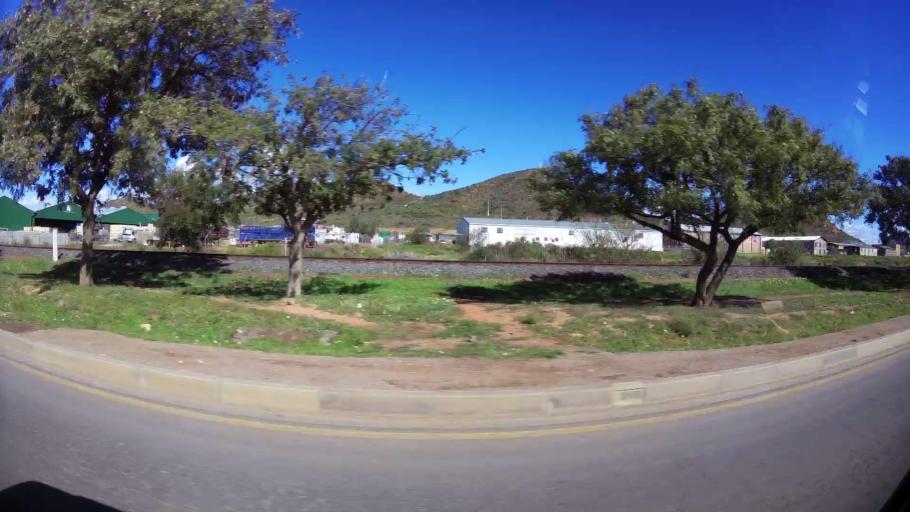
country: ZA
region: Western Cape
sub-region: Cape Winelands District Municipality
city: Ashton
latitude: -33.8132
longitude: 19.8875
